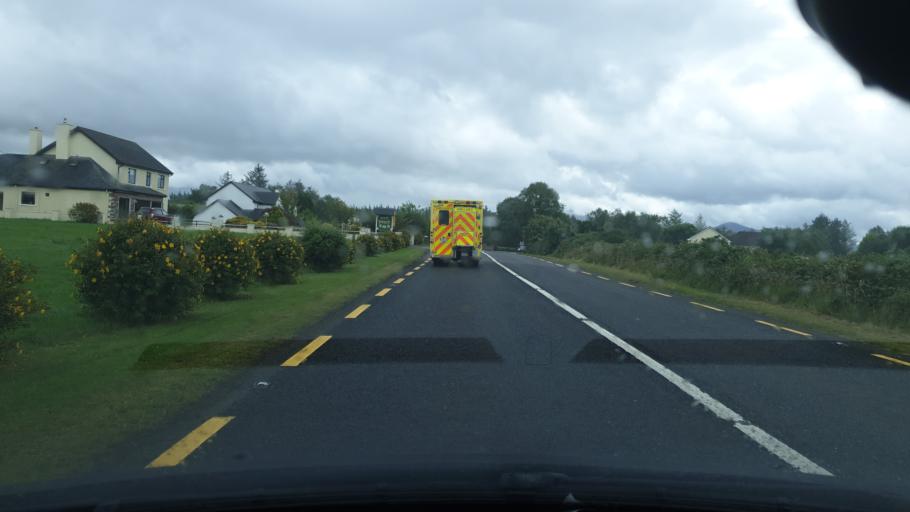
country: IE
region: Munster
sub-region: Ciarrai
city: Cill Airne
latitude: 52.0975
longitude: -9.5167
